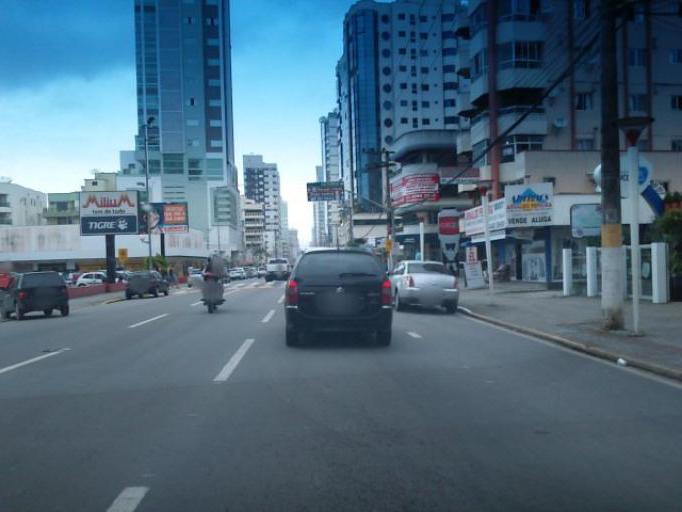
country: BR
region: Santa Catarina
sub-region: Itapema
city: Itapema
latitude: -27.1214
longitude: -48.6065
